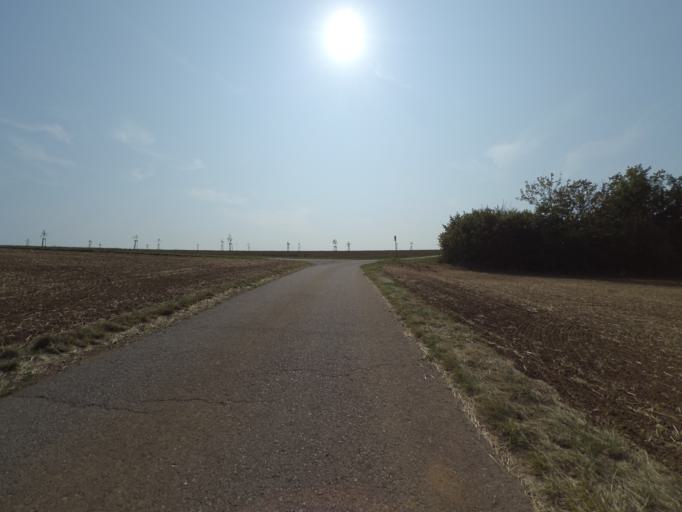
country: DE
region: Saarland
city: Perl
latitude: 49.4839
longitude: 6.4410
